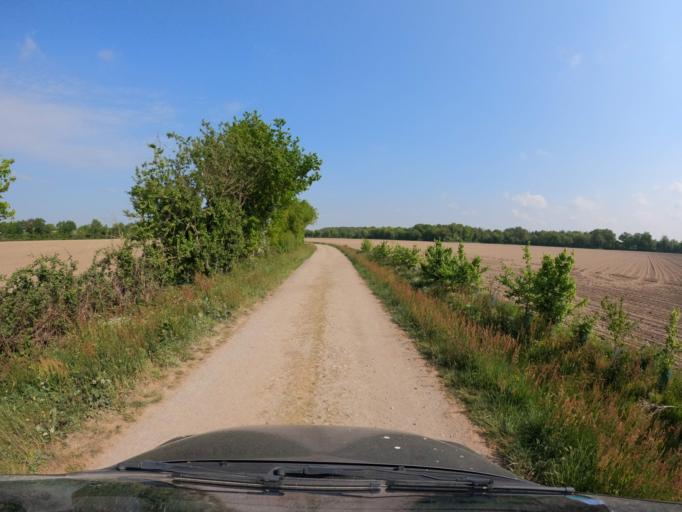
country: FR
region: Pays de la Loire
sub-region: Departement de la Vendee
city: Treize-Septiers
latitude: 47.0034
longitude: -1.2496
